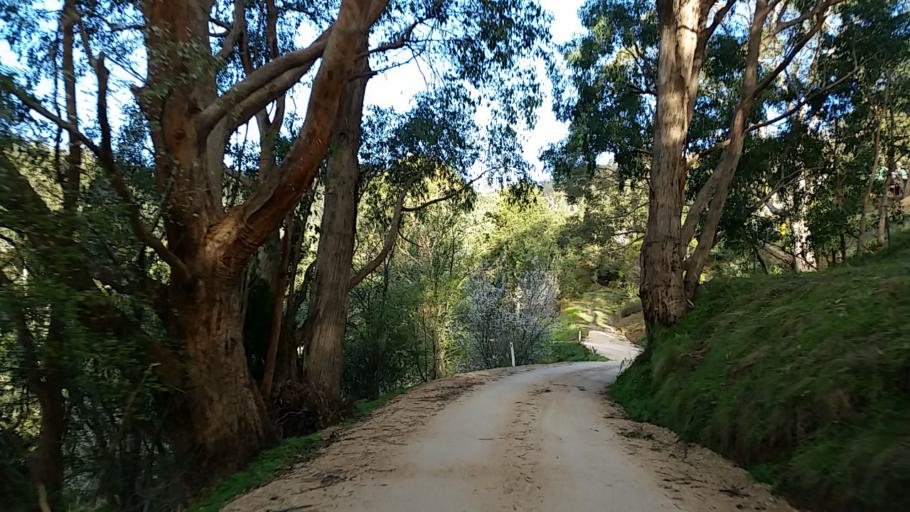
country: AU
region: South Australia
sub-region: Adelaide Hills
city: Balhannah
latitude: -34.9262
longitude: 138.7853
